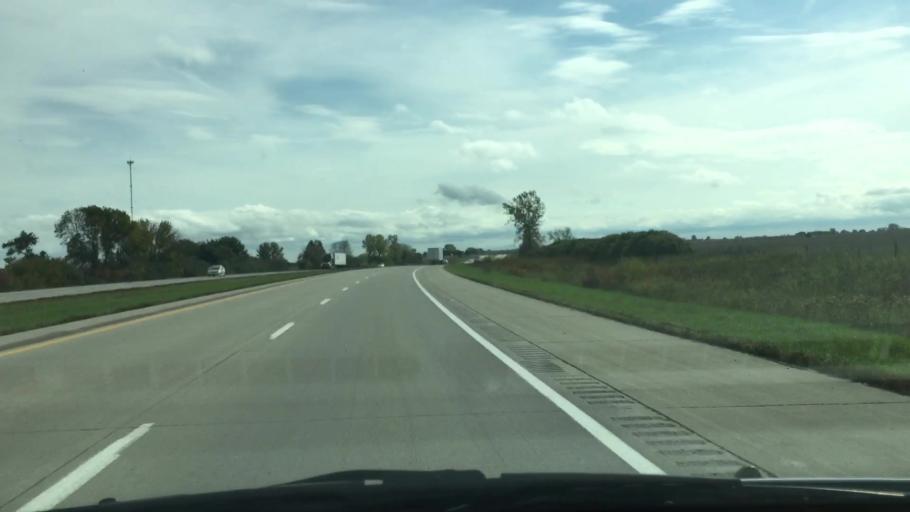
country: US
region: Iowa
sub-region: Clarke County
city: Osceola
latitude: 40.9285
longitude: -93.7973
